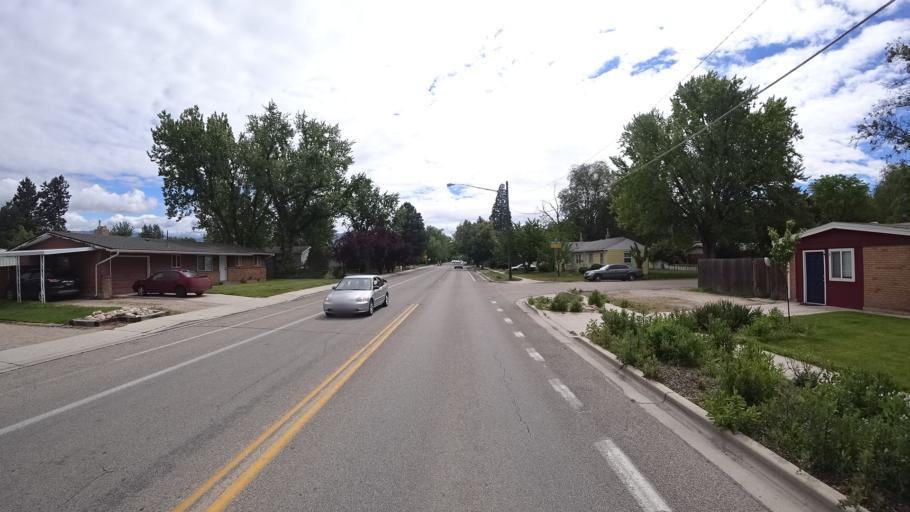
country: US
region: Idaho
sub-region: Ada County
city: Boise
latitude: 43.5790
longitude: -116.1926
